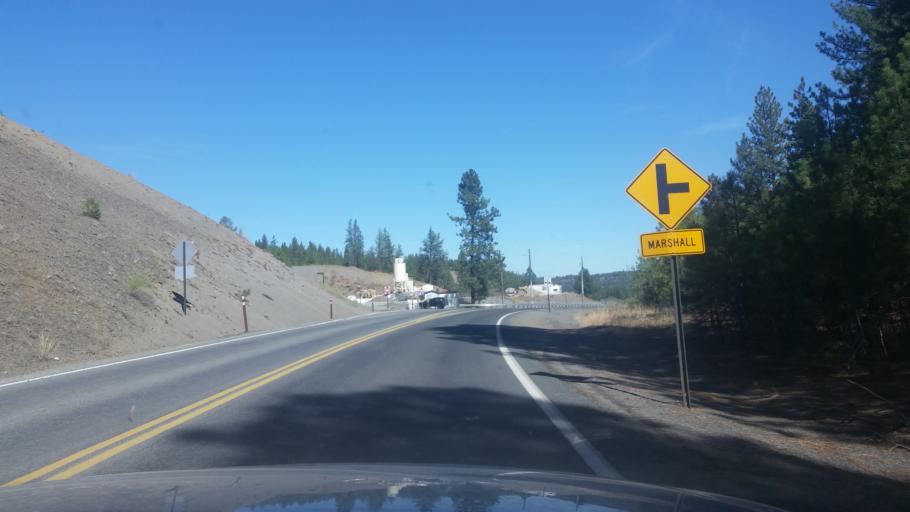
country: US
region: Washington
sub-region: Spokane County
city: Cheney
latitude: 47.5661
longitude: -117.4973
